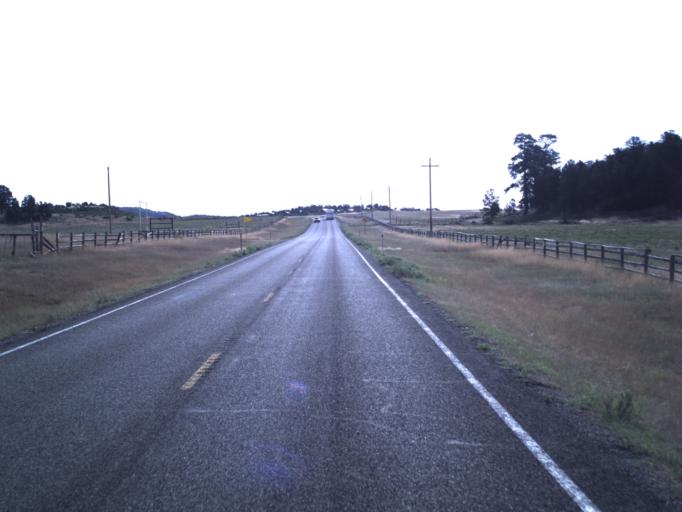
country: US
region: Utah
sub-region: Washington County
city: Hildale
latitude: 37.2419
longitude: -112.8163
